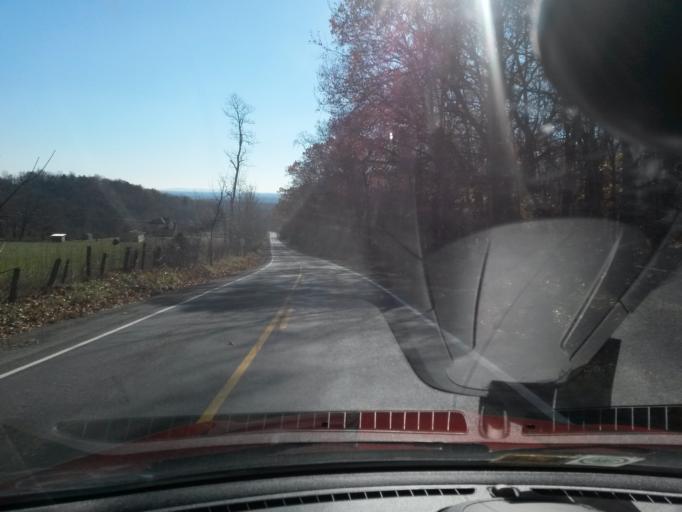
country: US
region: Virginia
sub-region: City of Bedford
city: Bedford
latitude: 37.4269
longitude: -79.5749
